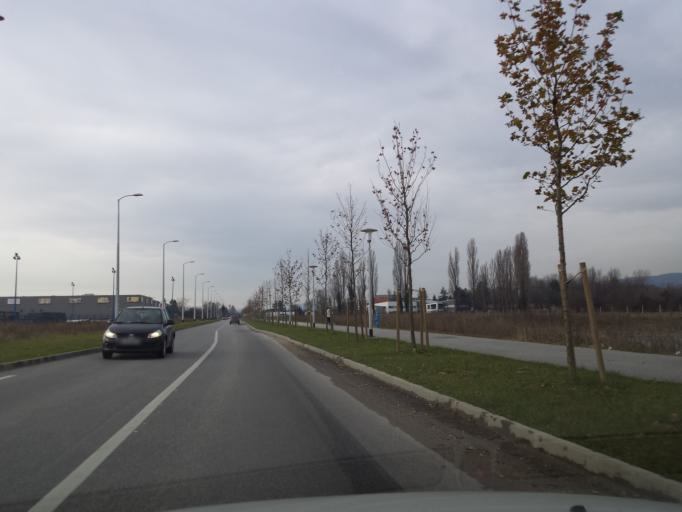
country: HR
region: Grad Zagreb
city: Stenjevec
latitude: 45.8037
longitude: 15.8816
